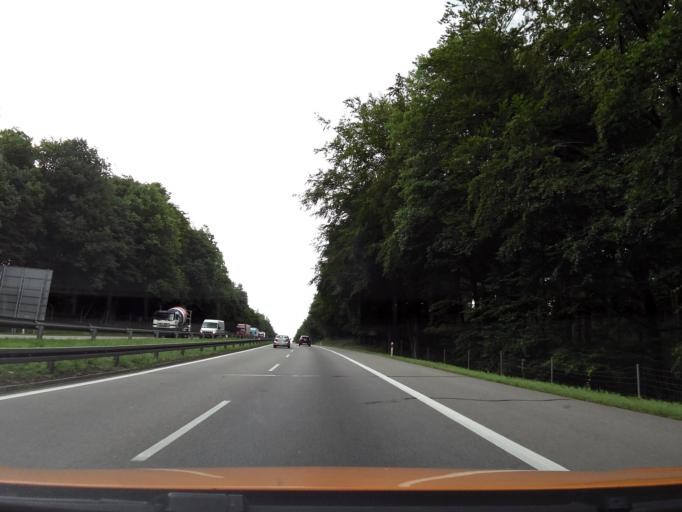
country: PL
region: West Pomeranian Voivodeship
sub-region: Szczecin
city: Szczecin
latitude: 53.3484
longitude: 14.5999
